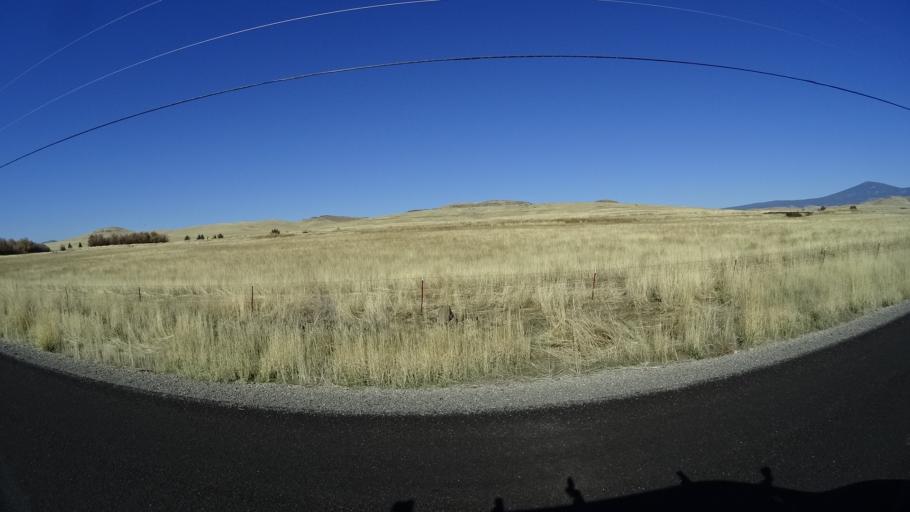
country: US
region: California
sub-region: Siskiyou County
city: Montague
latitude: 41.7262
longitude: -122.4247
